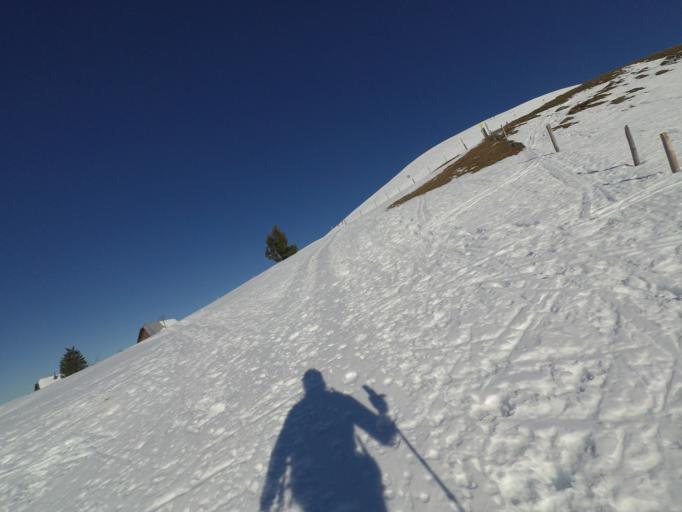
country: AT
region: Salzburg
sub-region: Politischer Bezirk Hallein
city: Scheffau am Tennengebirge
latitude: 47.6350
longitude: 13.2629
